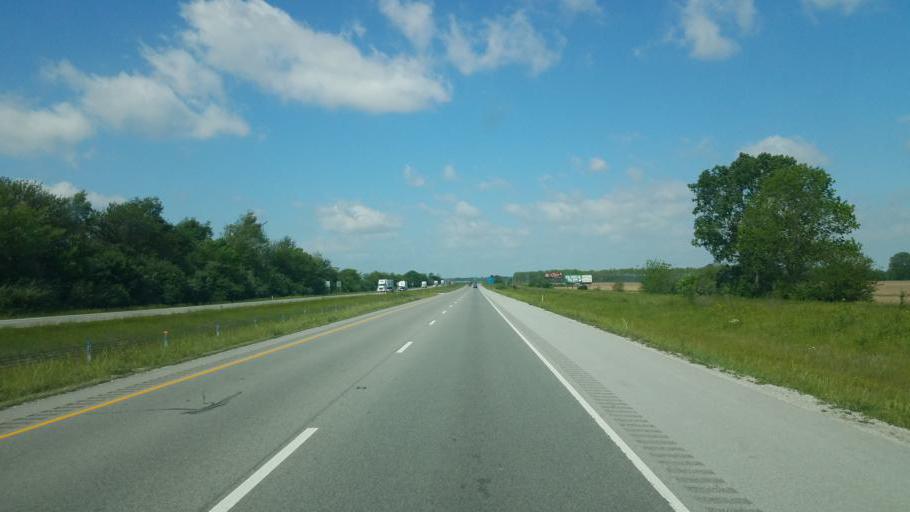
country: US
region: Indiana
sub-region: Morgan County
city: Monrovia
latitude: 39.5745
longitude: -86.6173
